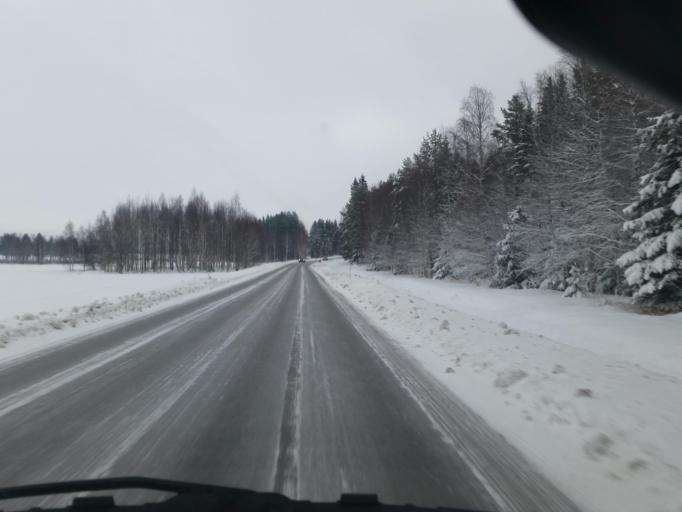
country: SE
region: Norrbotten
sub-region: Pitea Kommun
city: Roknas
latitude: 65.3192
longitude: 21.2724
